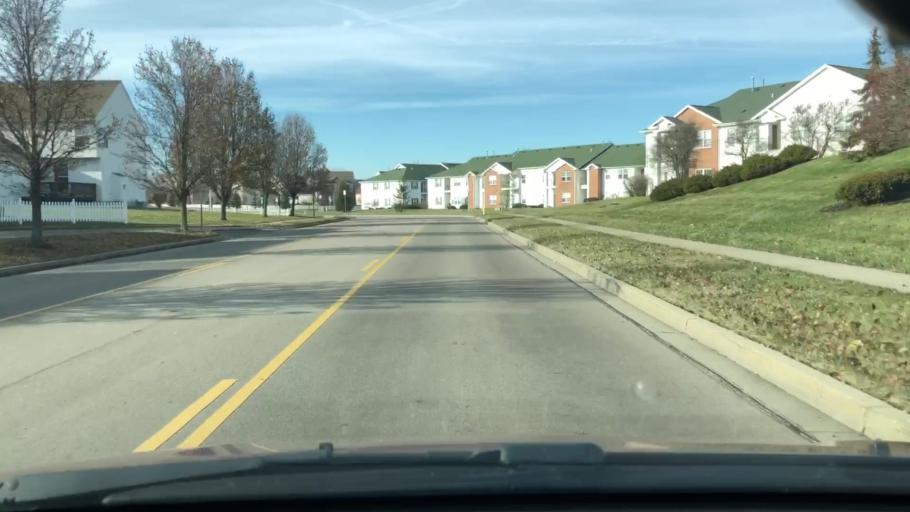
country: US
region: Ohio
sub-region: Greene County
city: Wright-Patterson AFB
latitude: 39.7656
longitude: -84.0622
